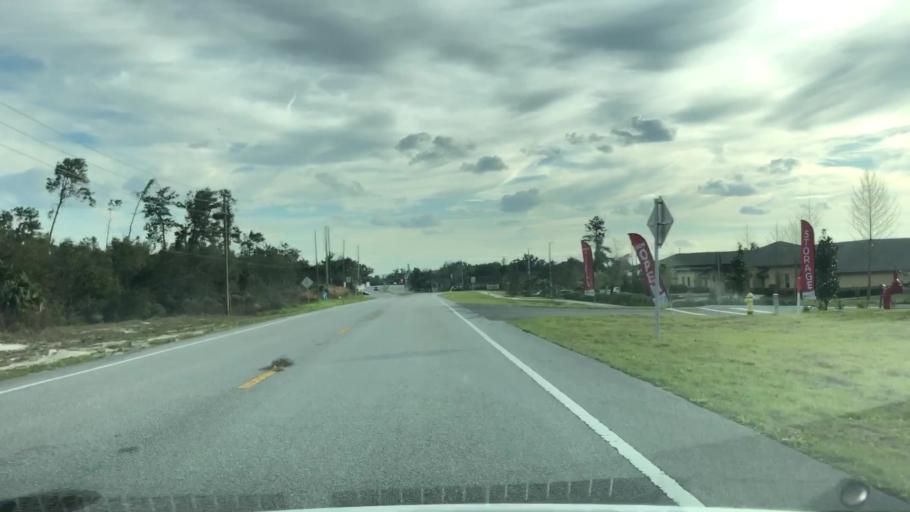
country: US
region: Florida
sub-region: Volusia County
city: Deltona
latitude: 28.9322
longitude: -81.2611
